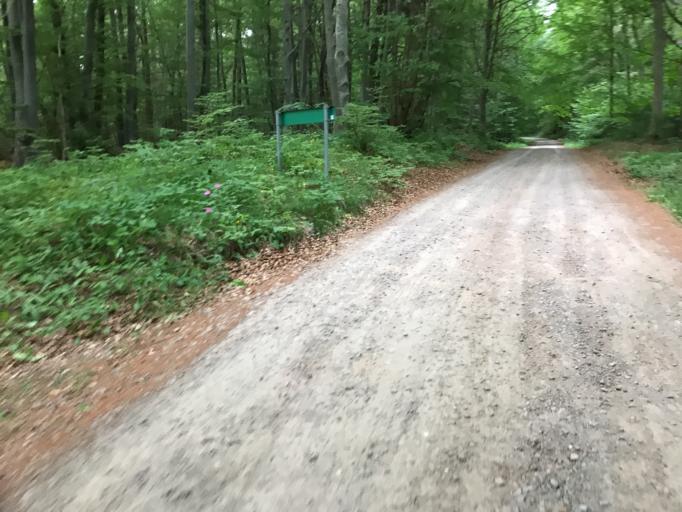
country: SE
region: OEstergoetland
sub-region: Odeshogs Kommun
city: OEdeshoeg
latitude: 58.3072
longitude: 14.6280
